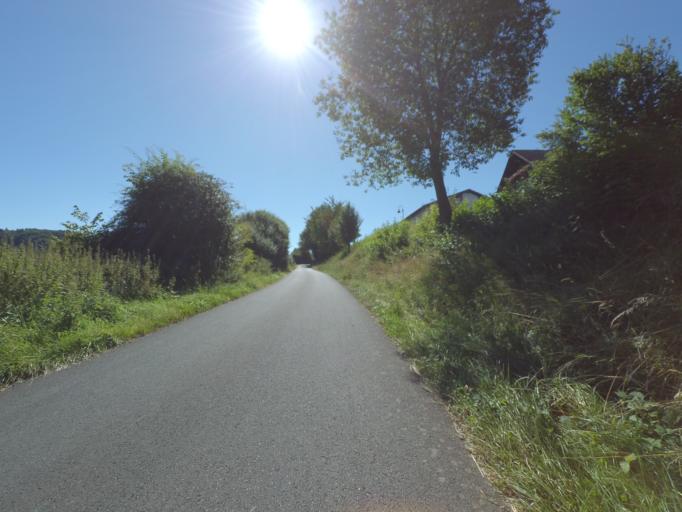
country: DE
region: Rheinland-Pfalz
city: Schonbach
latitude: 50.2130
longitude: 6.9492
